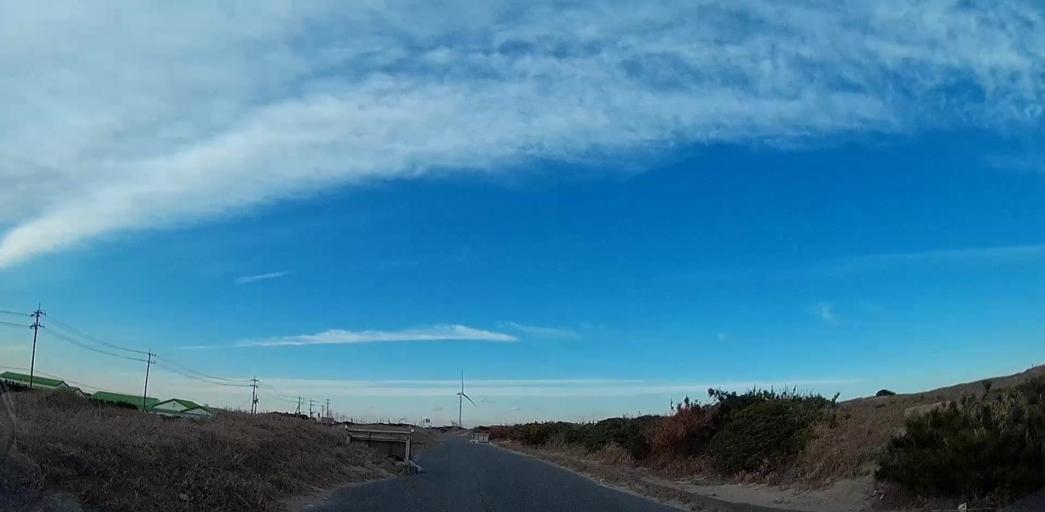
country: JP
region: Chiba
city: Hasaki
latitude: 35.7851
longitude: 140.8034
